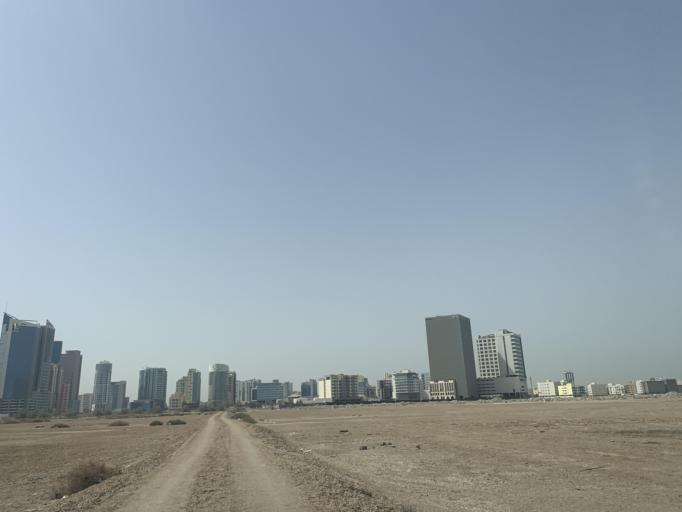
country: BH
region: Manama
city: Jidd Hafs
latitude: 26.2473
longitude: 50.5331
